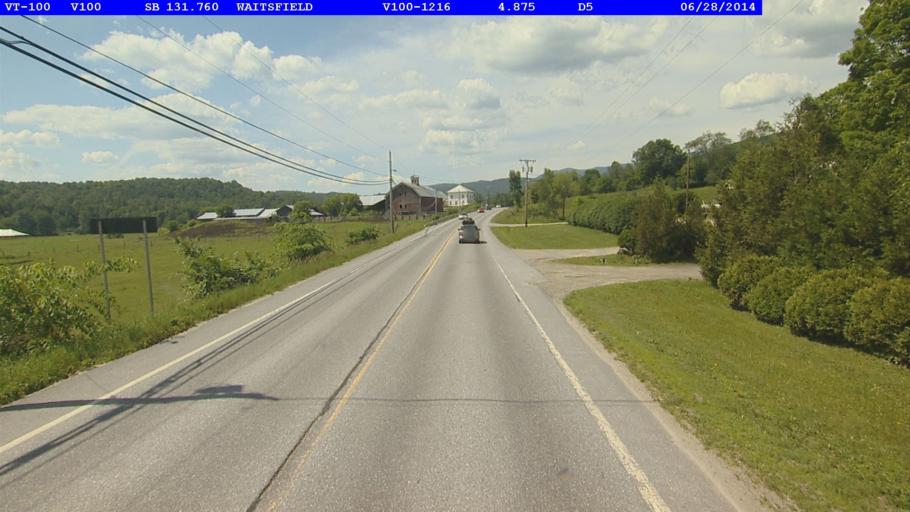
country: US
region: Vermont
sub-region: Washington County
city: Waterbury
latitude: 44.2041
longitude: -72.8091
